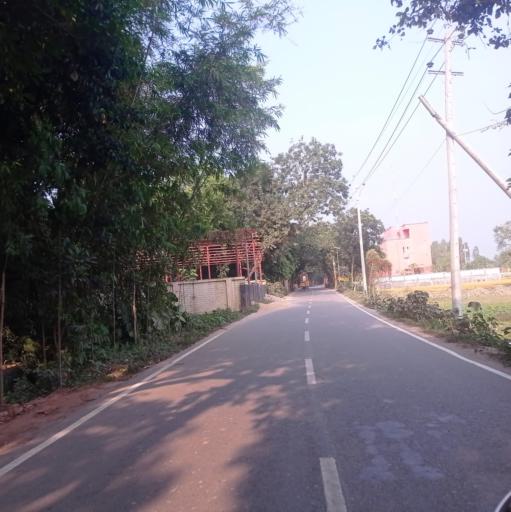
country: BD
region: Dhaka
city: Bhairab Bazar
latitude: 24.0930
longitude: 90.8509
